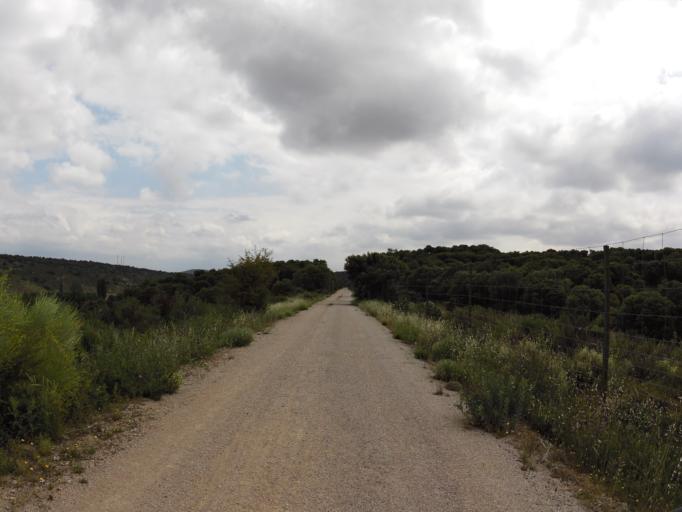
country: ES
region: Castille-La Mancha
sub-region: Provincia de Albacete
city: Robledo
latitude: 38.7718
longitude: -2.4087
